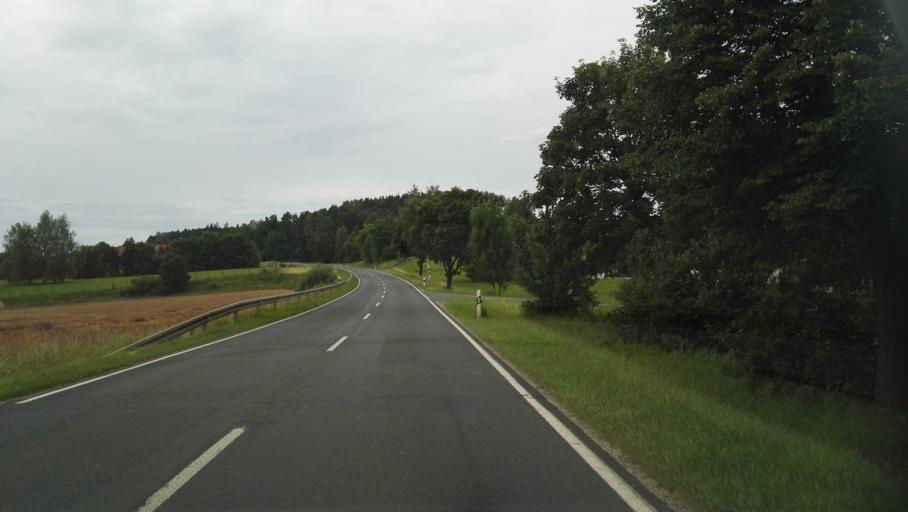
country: DE
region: Bavaria
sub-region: Upper Franconia
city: Plankenfels
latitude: 49.8965
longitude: 11.3331
